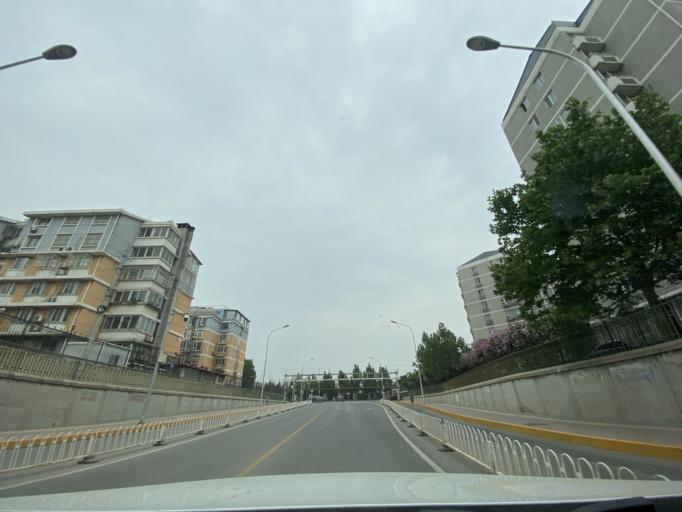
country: CN
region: Beijing
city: Sijiqing
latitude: 39.9319
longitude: 116.2422
